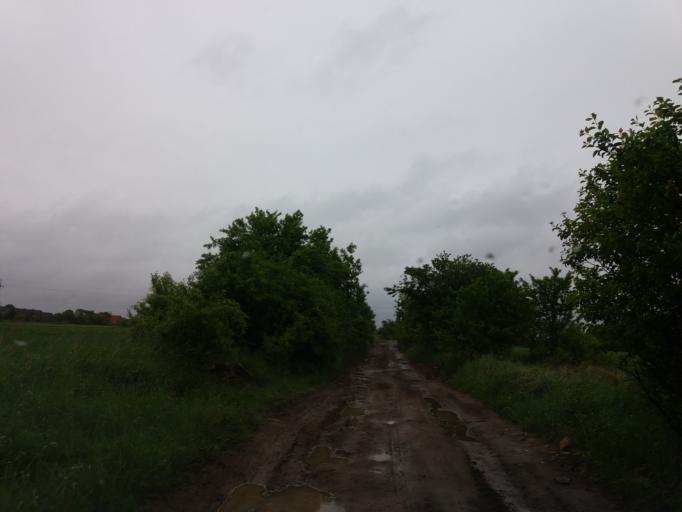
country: PL
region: Lubusz
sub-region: Powiat strzelecko-drezdenecki
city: Dobiegniew
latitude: 53.0191
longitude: 15.7944
